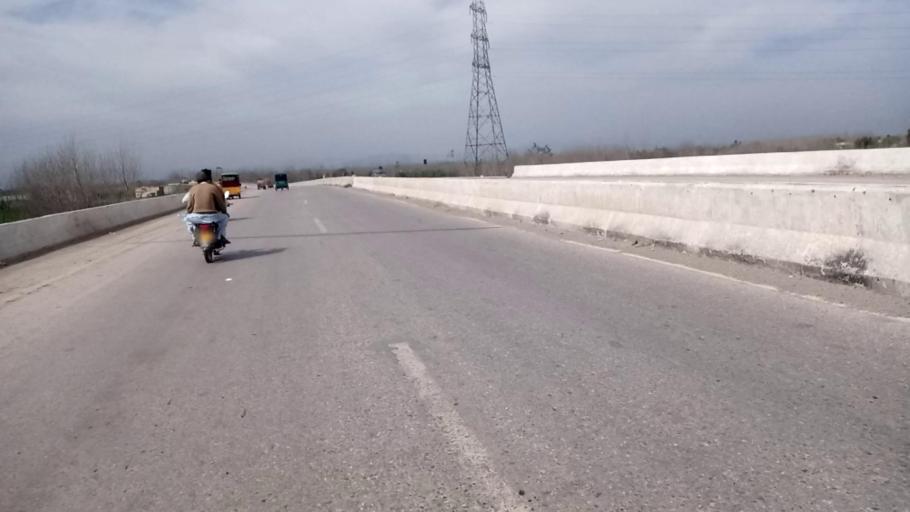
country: PK
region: Khyber Pakhtunkhwa
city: Peshawar
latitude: 34.0560
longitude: 71.6109
